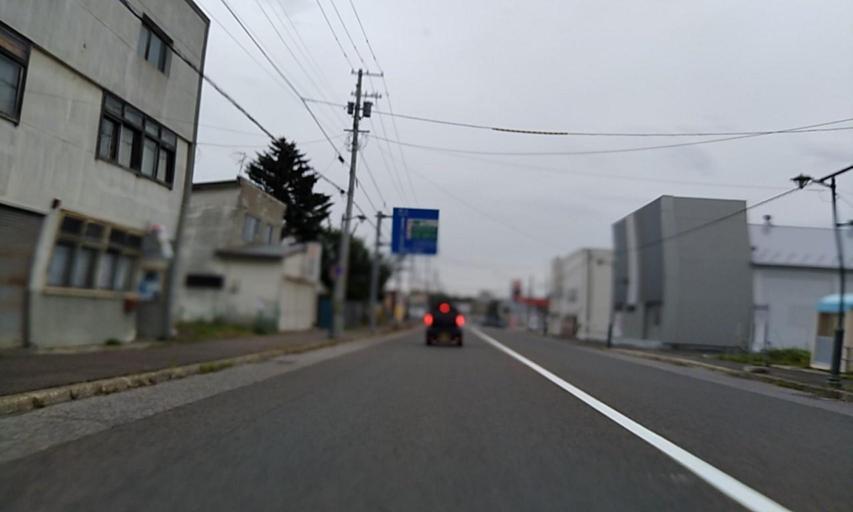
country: JP
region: Hokkaido
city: Bihoro
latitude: 43.9145
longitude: 144.1733
